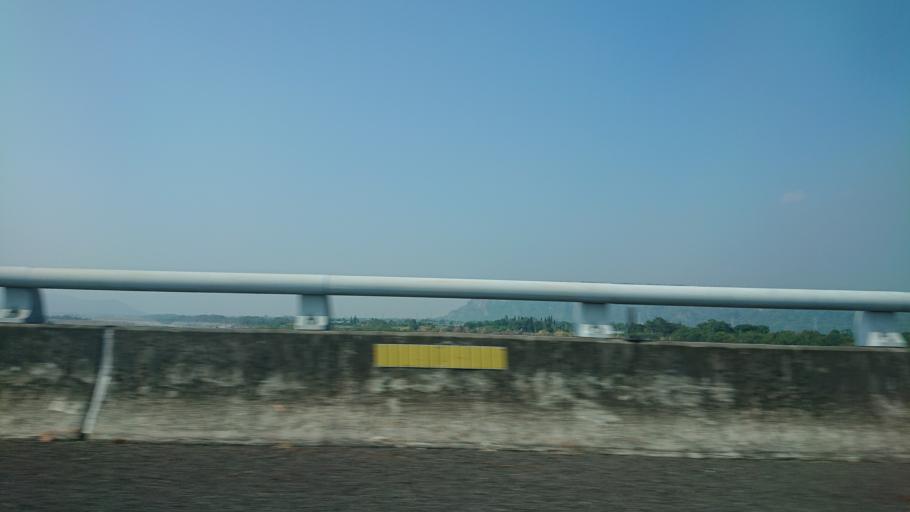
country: TW
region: Taiwan
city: Lugu
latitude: 23.8066
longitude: 120.6973
